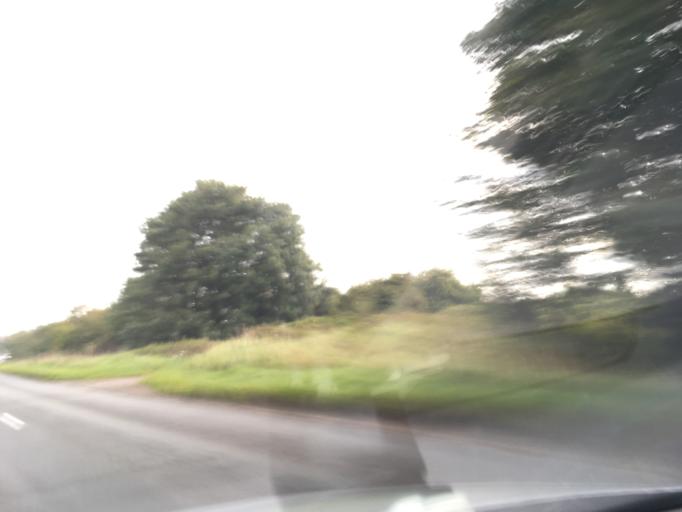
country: GB
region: England
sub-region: Oxfordshire
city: Cowley
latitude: 51.7809
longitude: -1.1834
